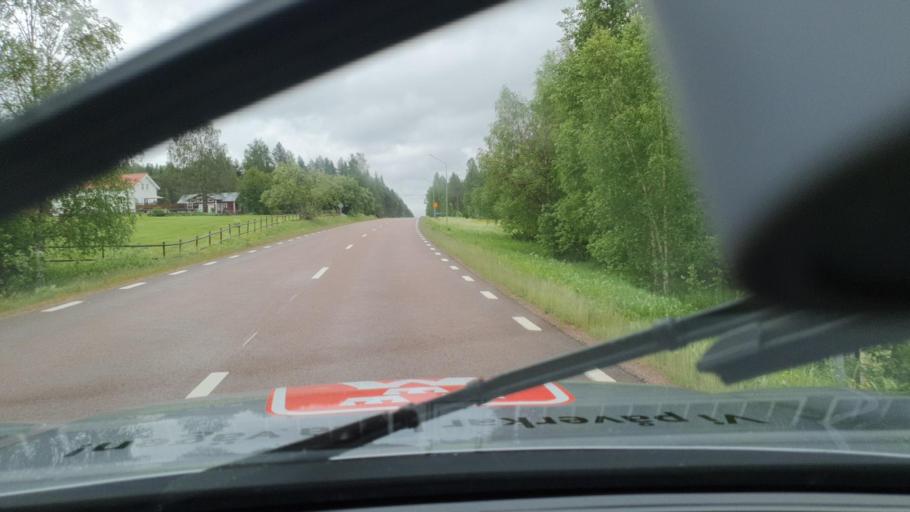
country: FI
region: Lapland
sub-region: Torniolaakso
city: Ylitornio
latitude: 66.1624
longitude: 23.8569
